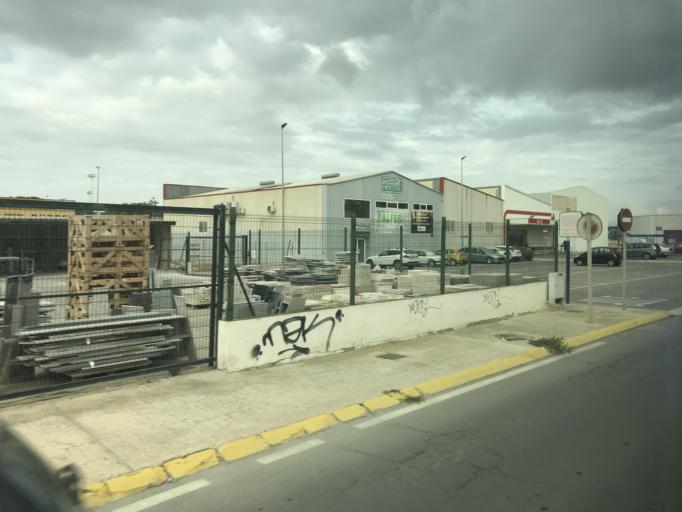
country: ES
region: Valencia
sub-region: Provincia de Alicante
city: Guardamar del Segura
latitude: 38.0899
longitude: -0.6595
